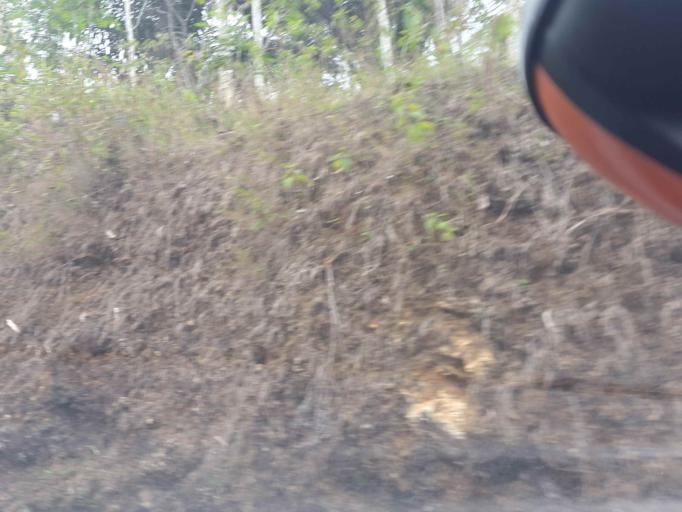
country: ID
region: East Java
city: Ploso
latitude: -8.0425
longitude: 111.1324
